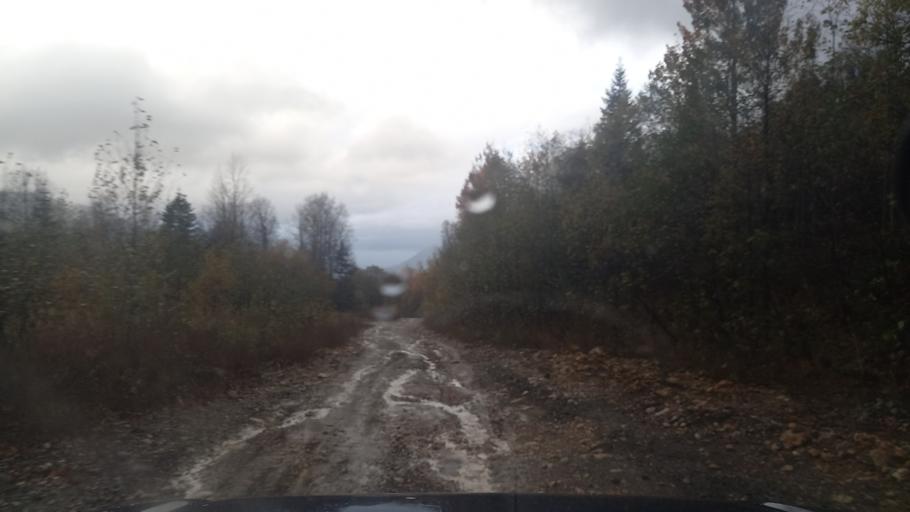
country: RU
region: Krasnodarskiy
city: Dagomys
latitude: 44.0000
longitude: 39.8481
